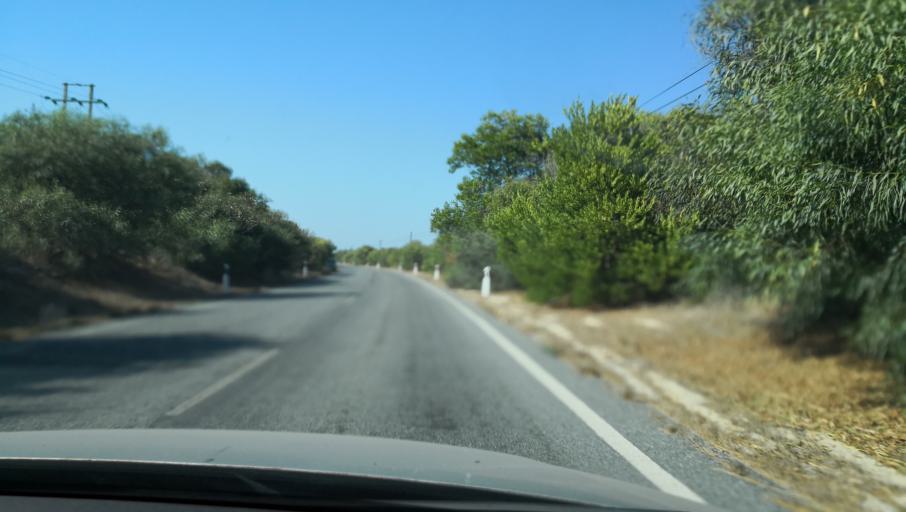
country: PT
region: Setubal
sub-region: Setubal
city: Setubal
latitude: 38.4020
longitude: -8.8071
